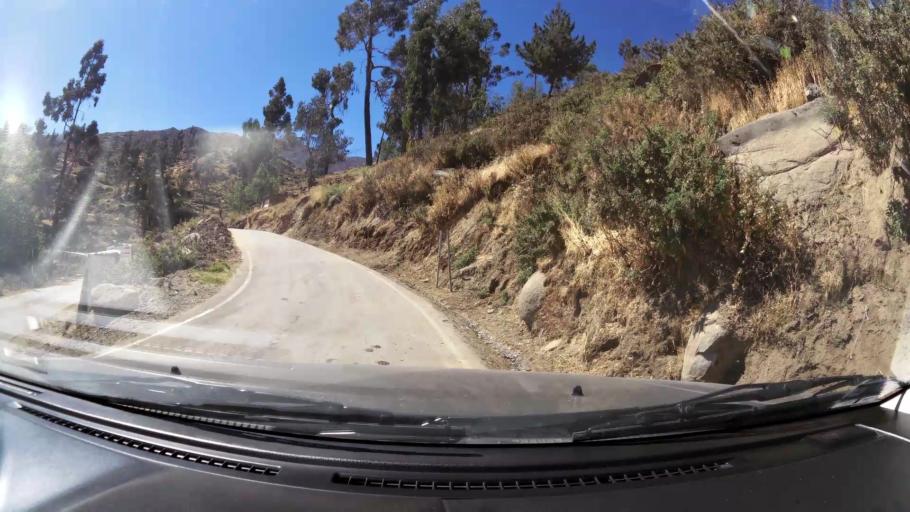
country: PE
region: Huancavelica
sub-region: Huaytara
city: Quito-Arma
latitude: -13.6845
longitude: -75.3741
